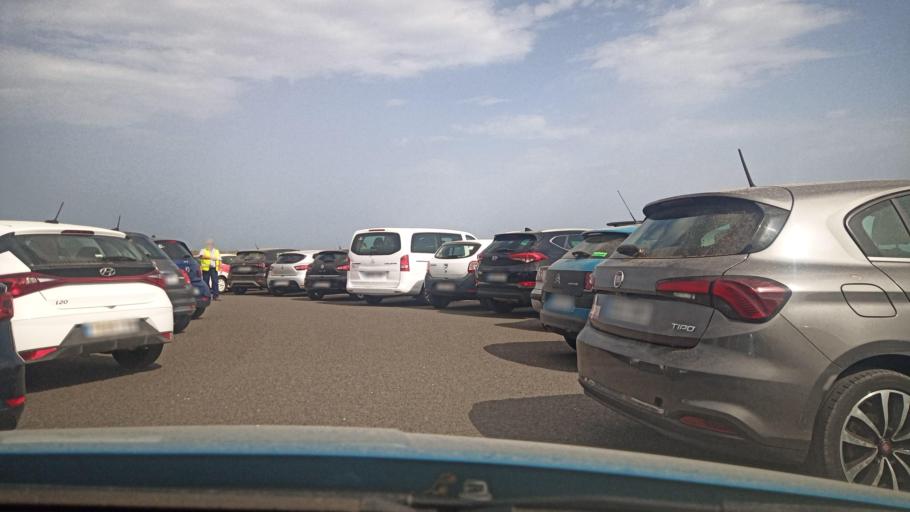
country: ES
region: Canary Islands
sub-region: Provincia de Las Palmas
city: Haria
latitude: 29.1607
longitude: -13.4383
